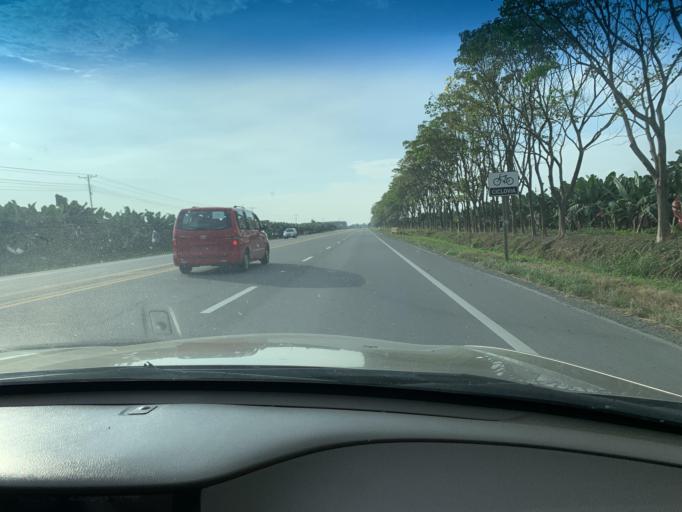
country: EC
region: Guayas
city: Coronel Marcelino Mariduena
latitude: -2.2694
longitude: -79.5411
